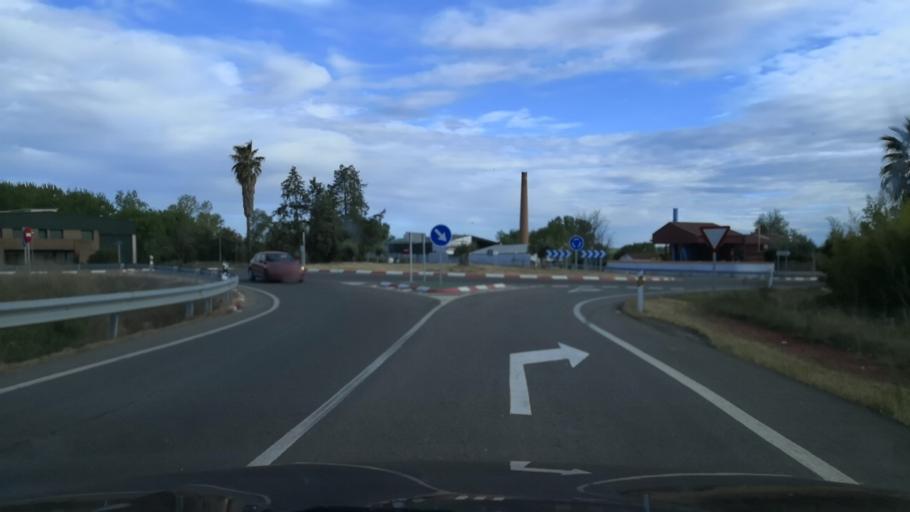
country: ES
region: Extremadura
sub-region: Provincia de Caceres
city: Moraleja
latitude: 40.0782
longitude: -6.6686
